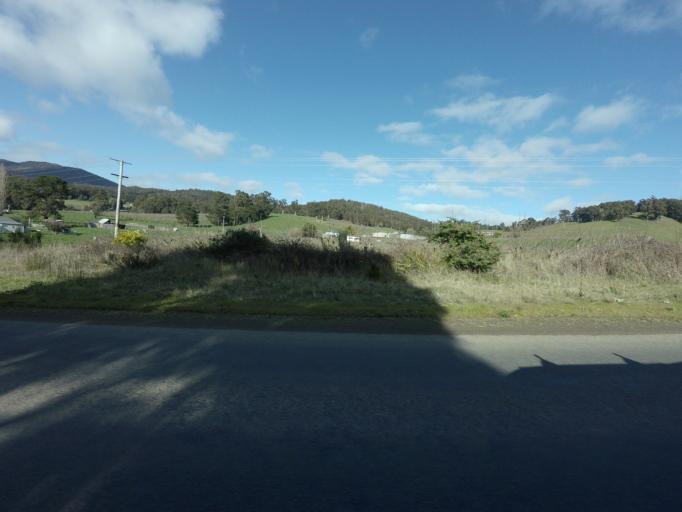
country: AU
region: Tasmania
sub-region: Huon Valley
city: Geeveston
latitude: -43.1888
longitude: 146.9586
